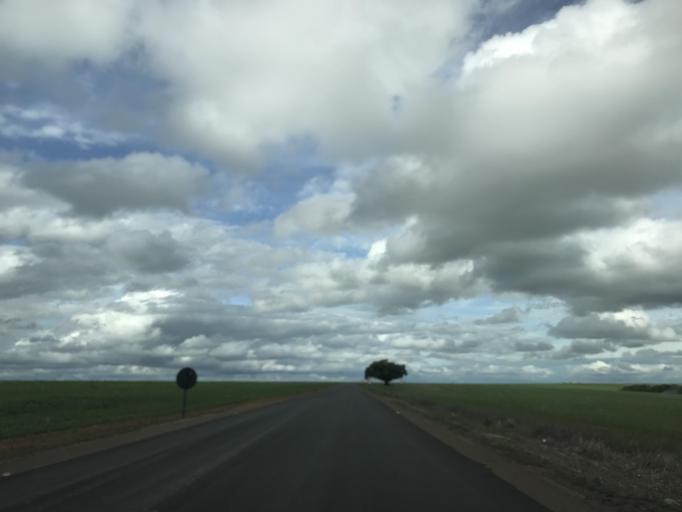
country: BR
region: Goias
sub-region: Vianopolis
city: Vianopolis
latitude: -16.9623
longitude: -48.6416
